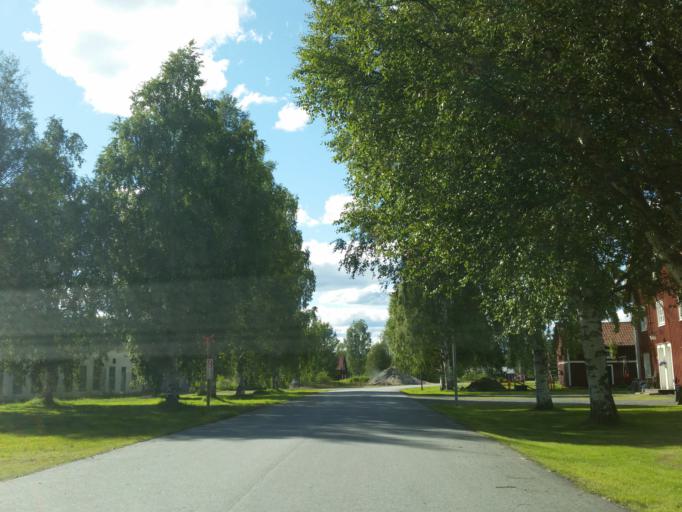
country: SE
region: Vaesterbotten
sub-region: Robertsfors Kommun
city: Robertsfors
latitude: 64.1856
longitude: 20.8478
